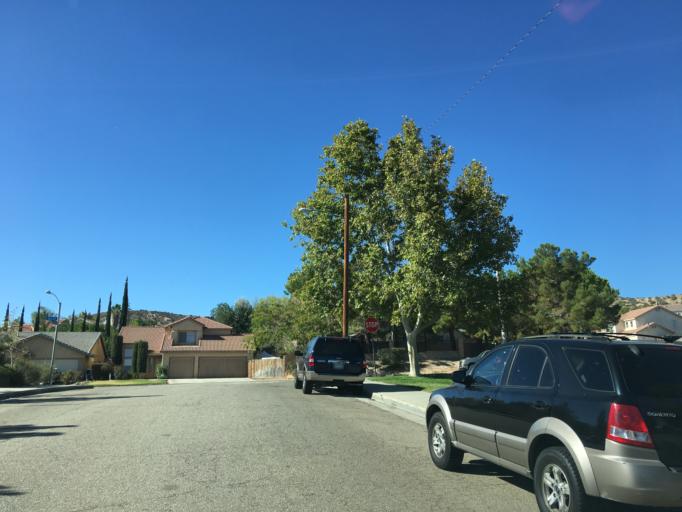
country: US
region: California
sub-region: Los Angeles County
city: Desert View Highlands
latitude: 34.5847
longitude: -118.1540
